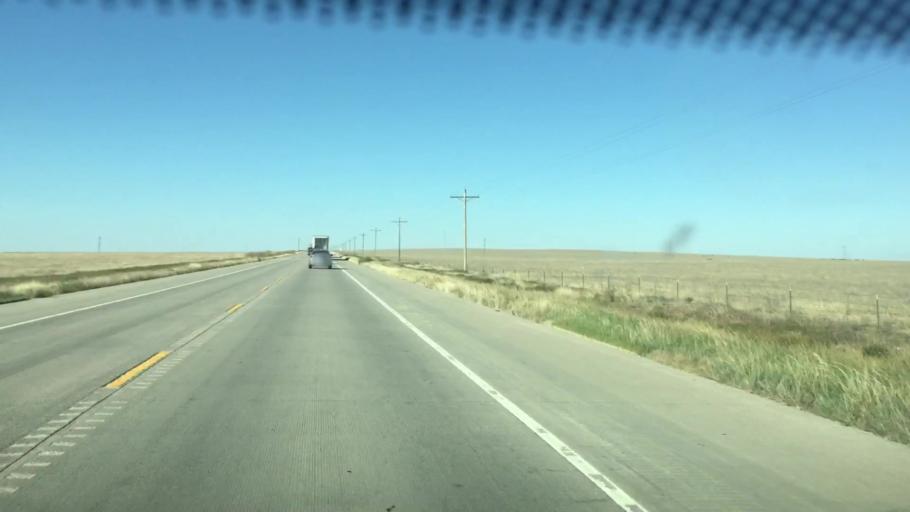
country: US
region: Colorado
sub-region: Prowers County
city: Lamar
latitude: 38.2533
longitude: -102.7239
